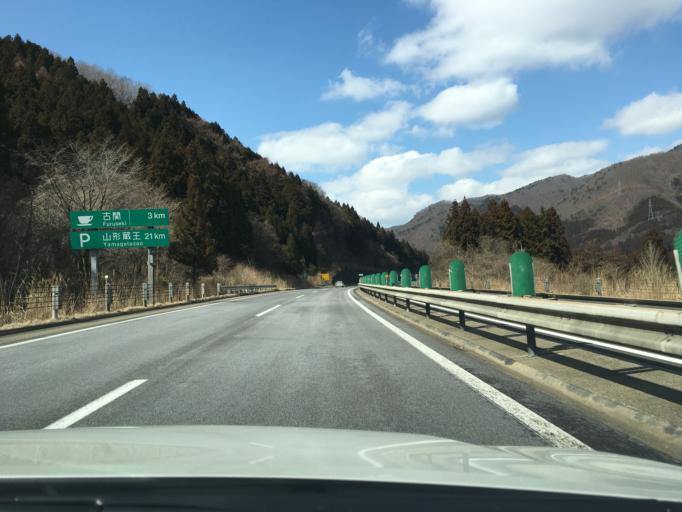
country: JP
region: Miyagi
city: Shiroishi
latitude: 38.1997
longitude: 140.5841
